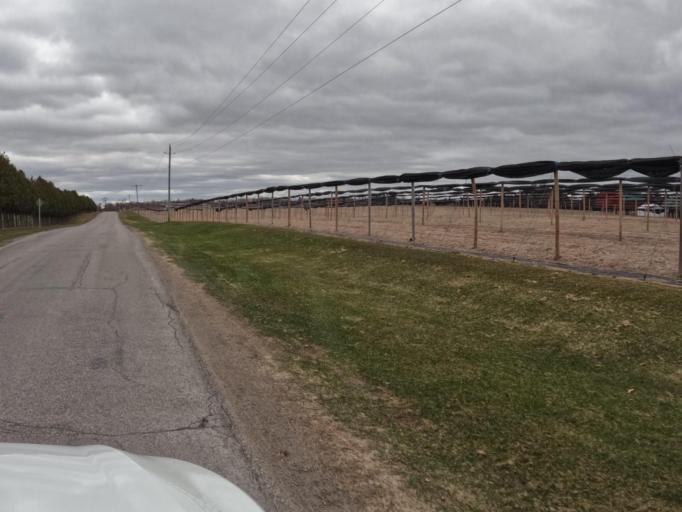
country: CA
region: Ontario
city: Norfolk County
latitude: 42.9609
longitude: -80.3966
